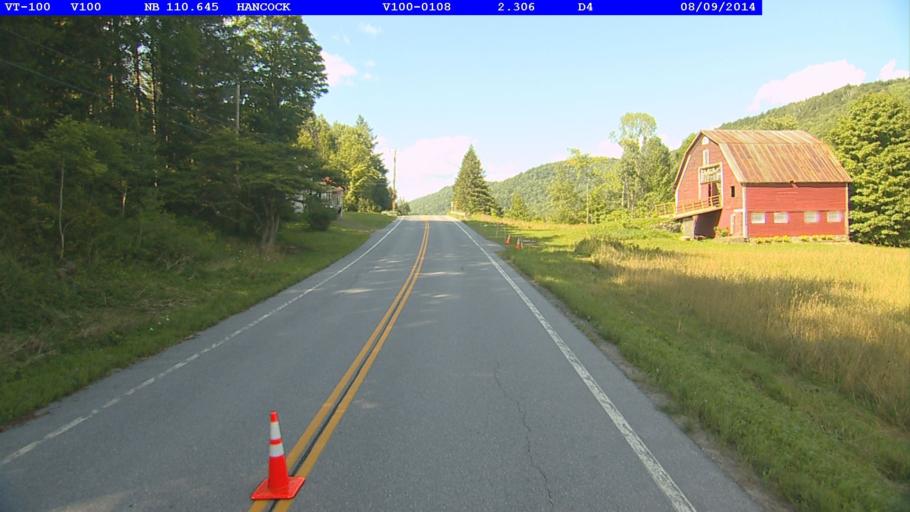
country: US
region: Vermont
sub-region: Orange County
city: Randolph
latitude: 43.9418
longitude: -72.8414
